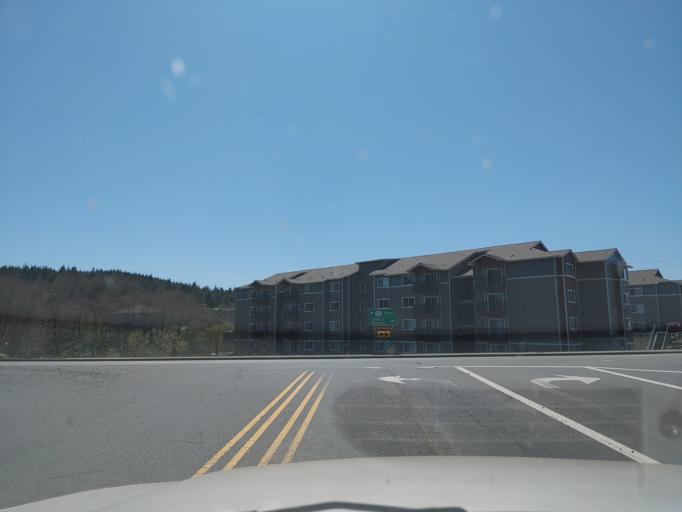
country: US
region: Oregon
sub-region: Clatsop County
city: Warrenton
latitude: 46.1451
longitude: -123.9017
